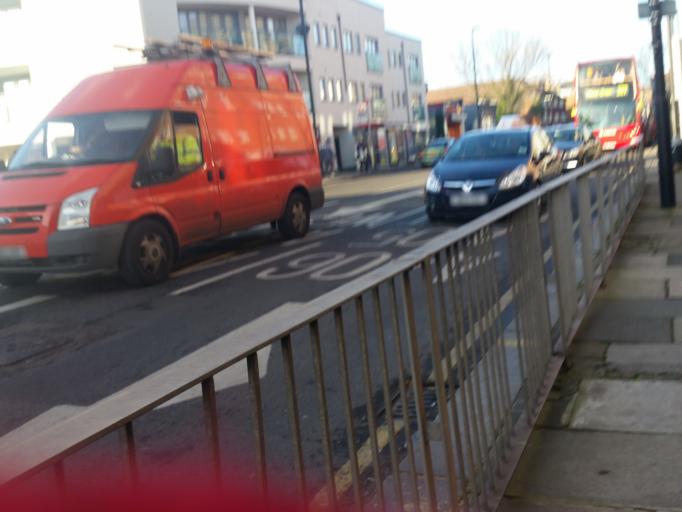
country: GB
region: England
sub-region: Greater London
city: Wood Green
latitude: 51.6130
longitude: -0.1095
